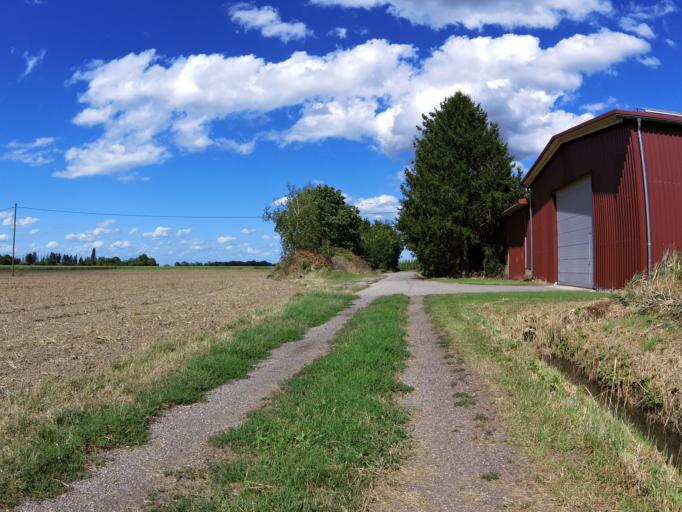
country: DE
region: Baden-Wuerttemberg
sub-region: Freiburg Region
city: Lahr
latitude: 48.3619
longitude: 7.8461
